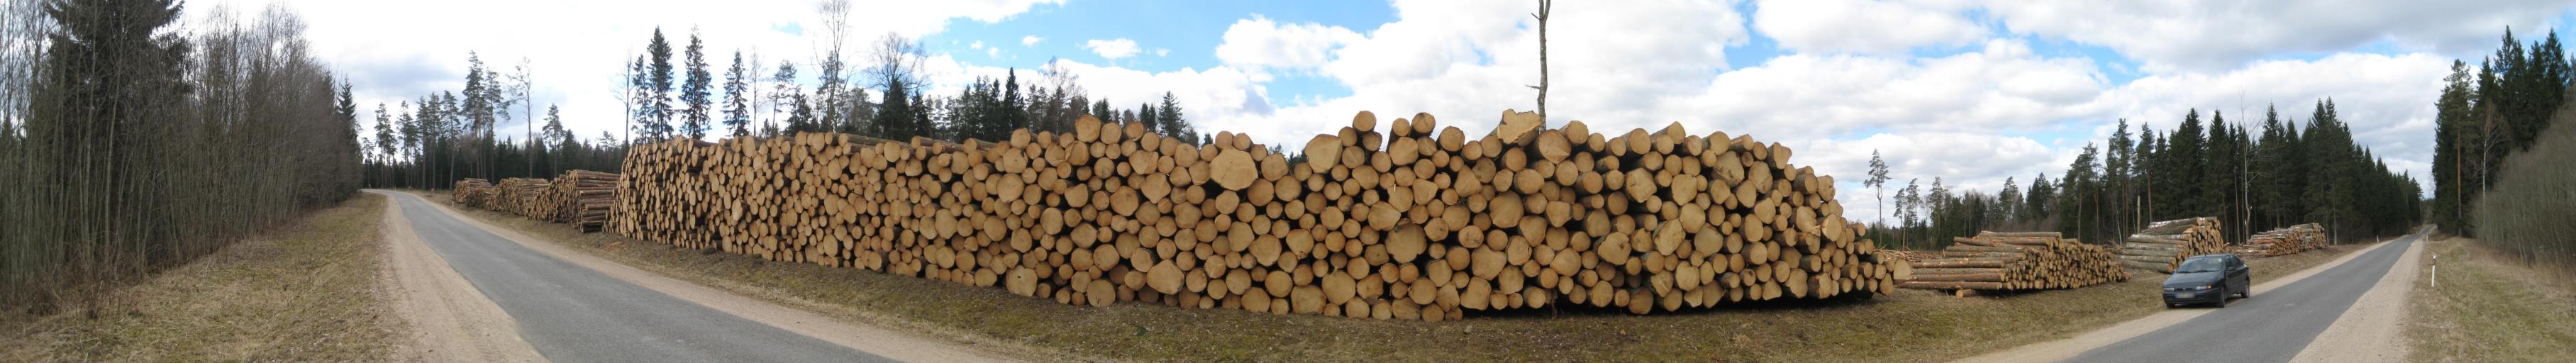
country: LT
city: Zarasai
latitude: 55.6750
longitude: 26.0154
